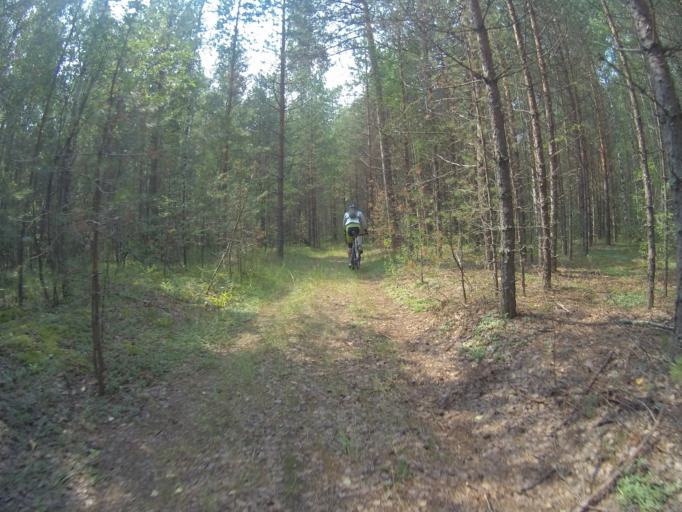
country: RU
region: Vladimir
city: Raduzhnyy
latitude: 55.9679
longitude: 40.2139
